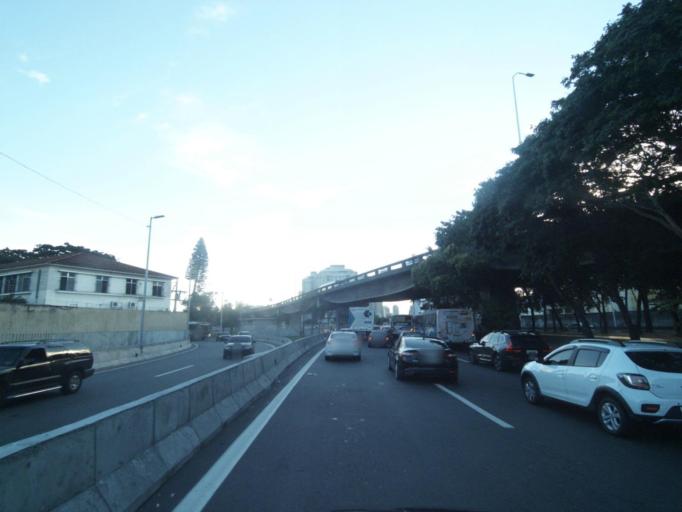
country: BR
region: Rio de Janeiro
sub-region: Niteroi
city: Niteroi
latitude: -22.8823
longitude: -43.1146
